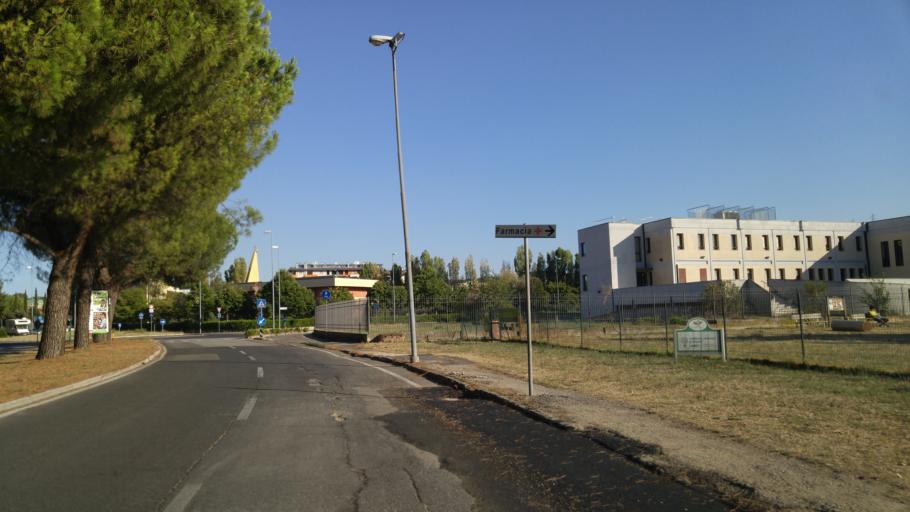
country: IT
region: The Marches
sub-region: Provincia di Pesaro e Urbino
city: Pesaro
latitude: 43.8936
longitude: 12.8989
